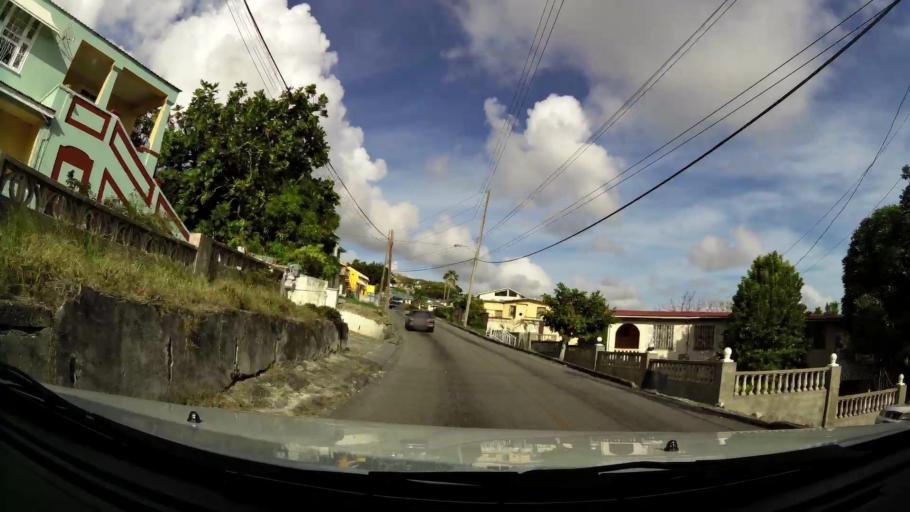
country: BB
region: Saint Michael
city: Bridgetown
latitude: 13.0865
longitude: -59.5869
